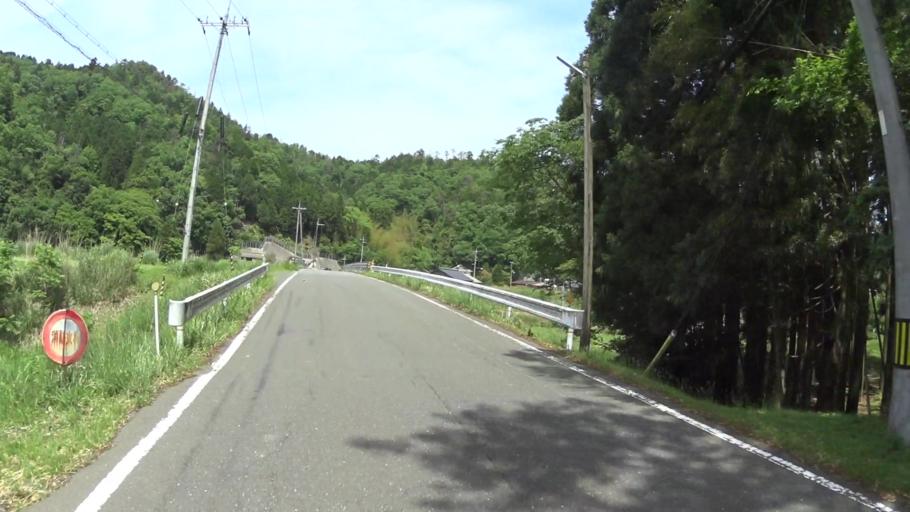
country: JP
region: Kyoto
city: Maizuru
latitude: 35.3852
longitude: 135.4559
